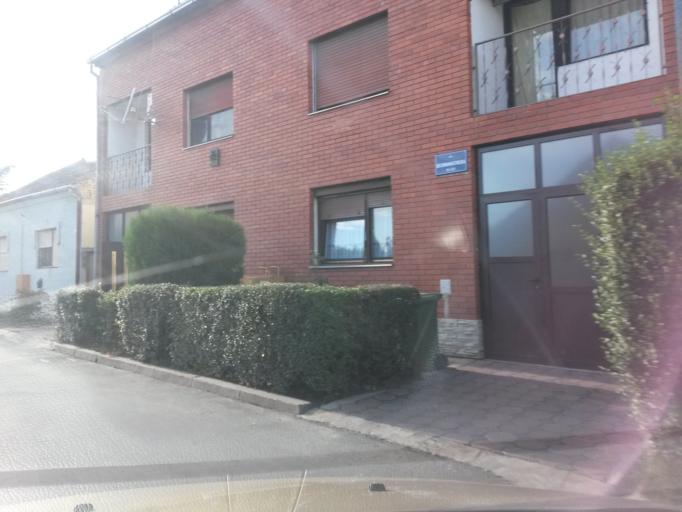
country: HR
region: Osjecko-Baranjska
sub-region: Grad Osijek
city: Osijek
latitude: 45.5490
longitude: 18.7031
